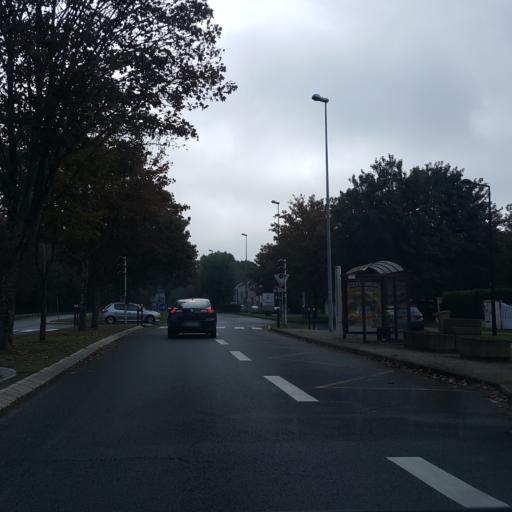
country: FR
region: Ile-de-France
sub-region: Departement de l'Essonne
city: Saint-Pierre-du-Perray
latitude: 48.6174
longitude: 2.4985
